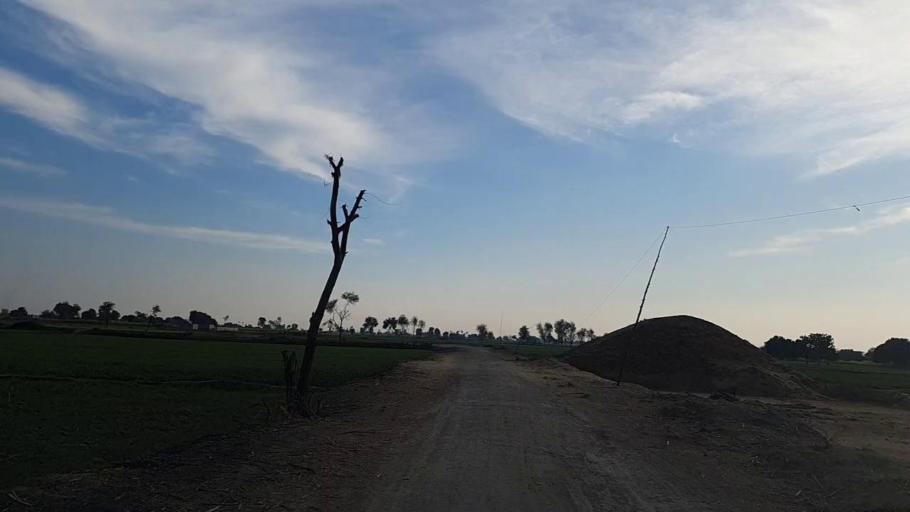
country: PK
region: Sindh
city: Bandhi
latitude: 26.5585
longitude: 68.2784
